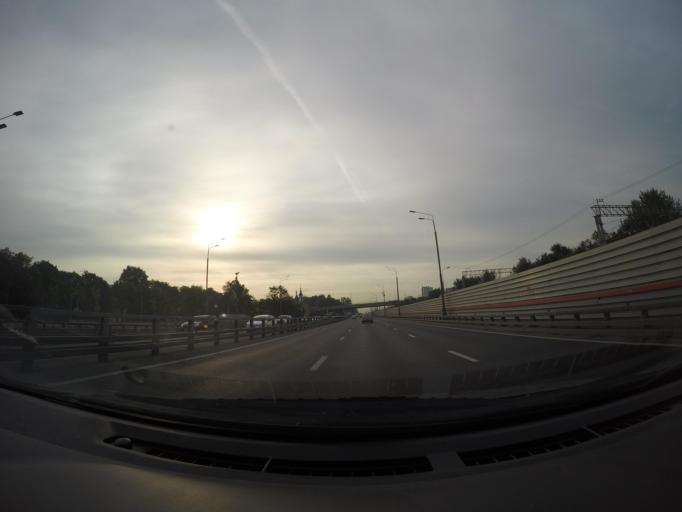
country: RU
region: Moscow
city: Perovo
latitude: 55.7246
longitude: 37.7933
